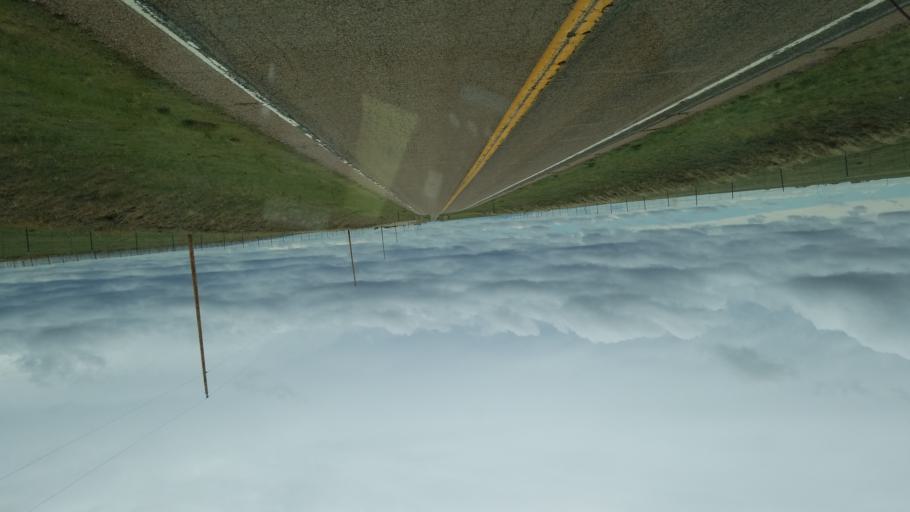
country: US
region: Colorado
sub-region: Lincoln County
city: Limon
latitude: 38.8382
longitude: -103.8605
